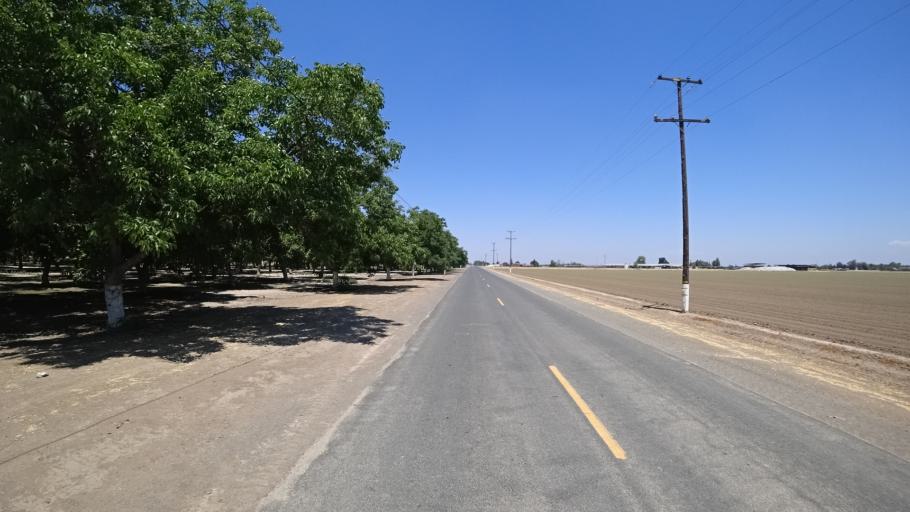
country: US
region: California
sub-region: Kings County
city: Armona
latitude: 36.3361
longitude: -119.7269
